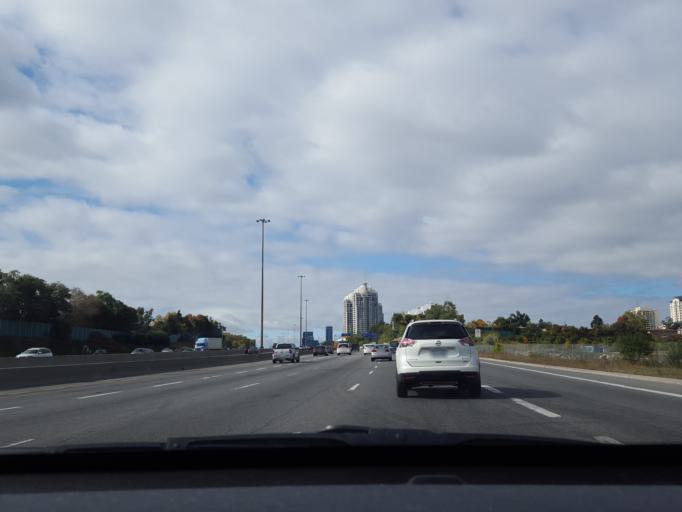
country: CA
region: Ontario
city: Willowdale
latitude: 43.7662
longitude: -79.3709
